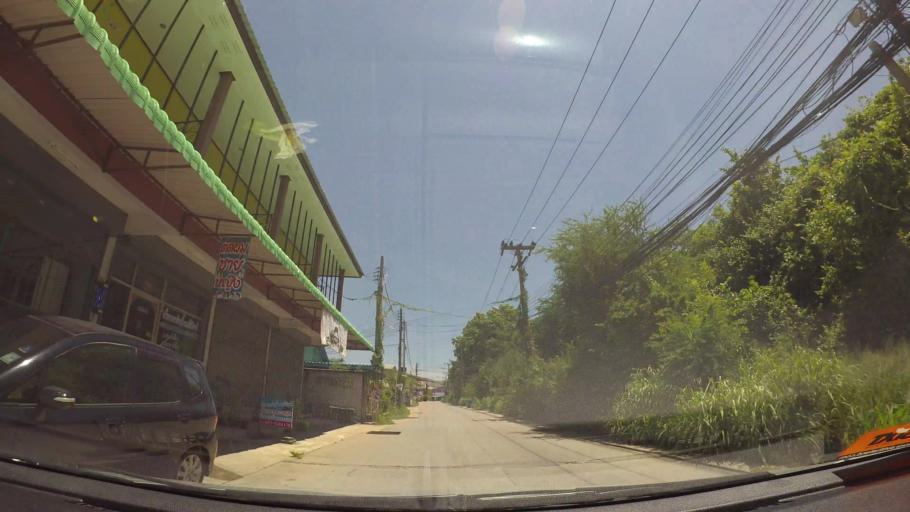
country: TH
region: Chon Buri
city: Si Racha
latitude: 13.1126
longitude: 100.9337
